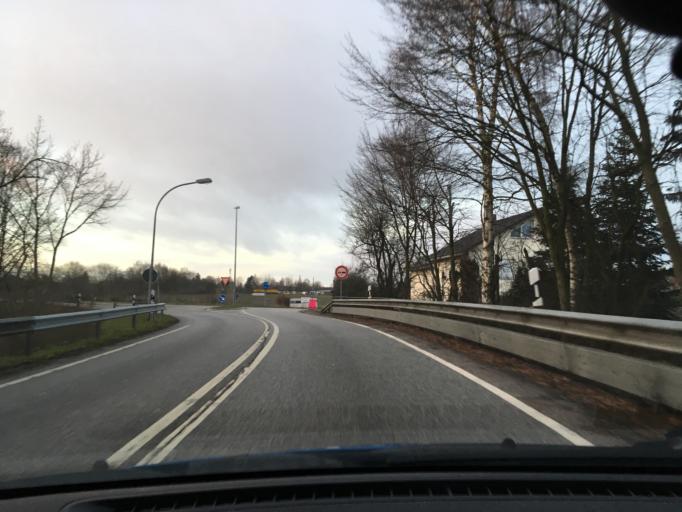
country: DE
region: Schleswig-Holstein
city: Pinneberg
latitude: 53.6787
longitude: 9.7995
